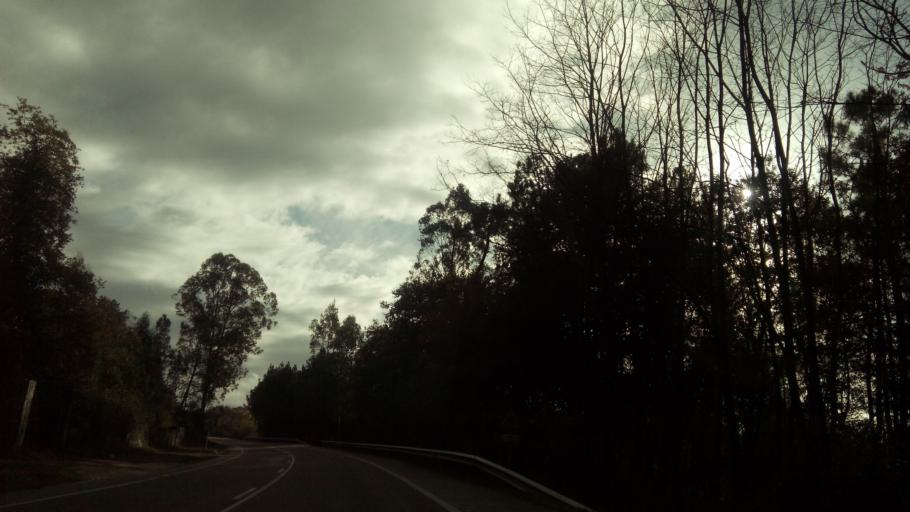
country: ES
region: Galicia
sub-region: Provincia de Pontevedra
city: Ponteareas
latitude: 42.1997
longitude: -8.5102
